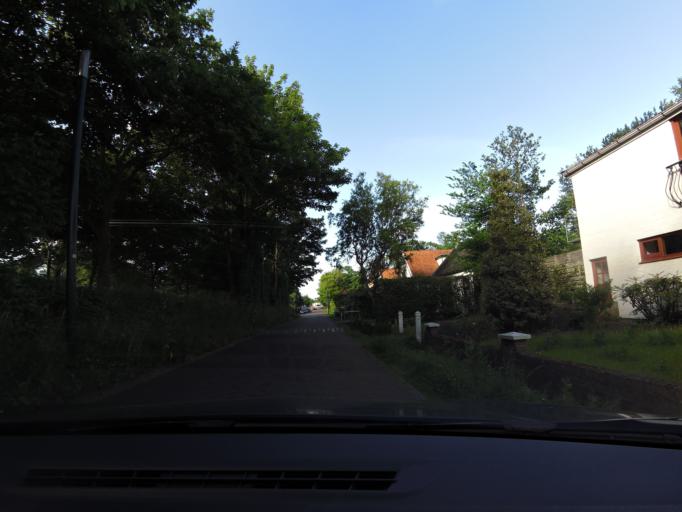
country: NL
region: Zeeland
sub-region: Schouwen-Duiveland
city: Renesse
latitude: 51.7349
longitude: 3.7771
